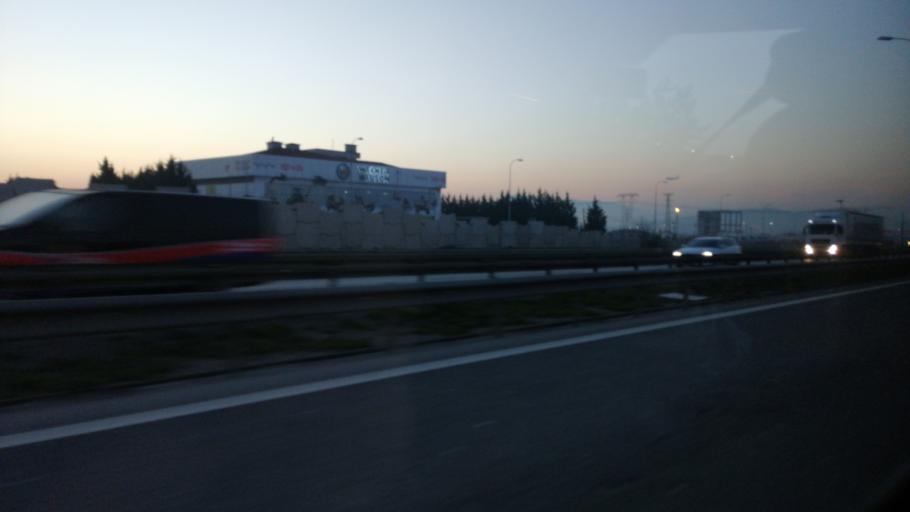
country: TR
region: Kocaeli
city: Balcik
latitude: 40.9041
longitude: 29.3646
